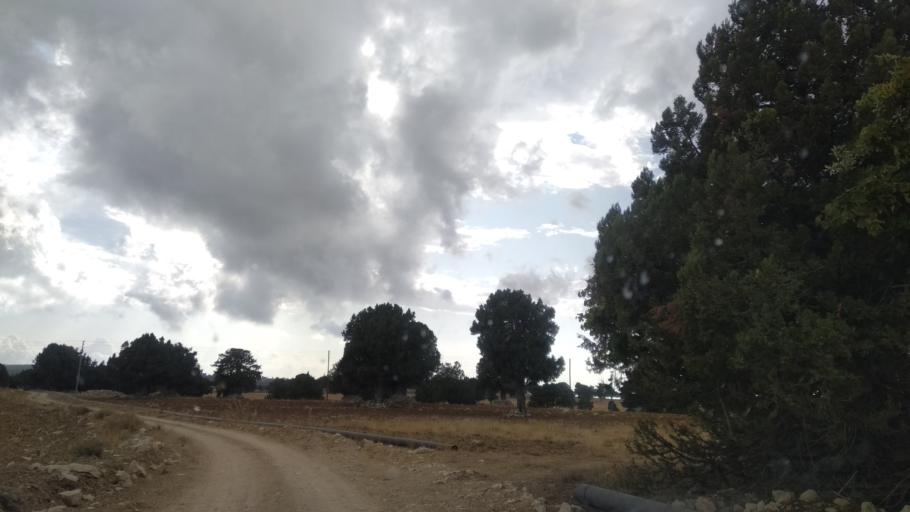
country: TR
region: Mersin
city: Sarikavak
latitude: 36.5701
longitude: 33.7455
